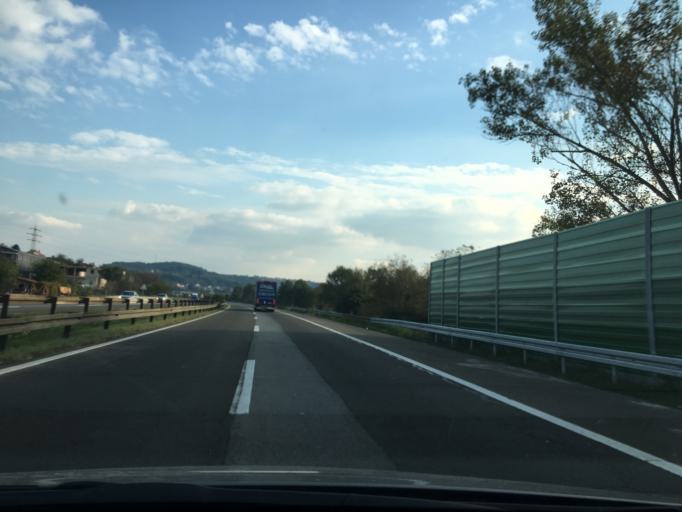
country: RS
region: Central Serbia
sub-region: Belgrade
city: Zvezdara
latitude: 44.6812
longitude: 20.5860
